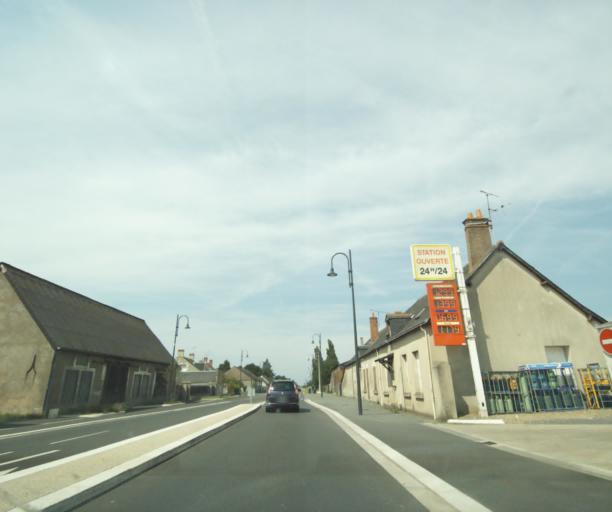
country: FR
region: Centre
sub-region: Departement d'Indre-et-Loire
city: Sorigny
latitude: 47.2436
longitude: 0.6950
